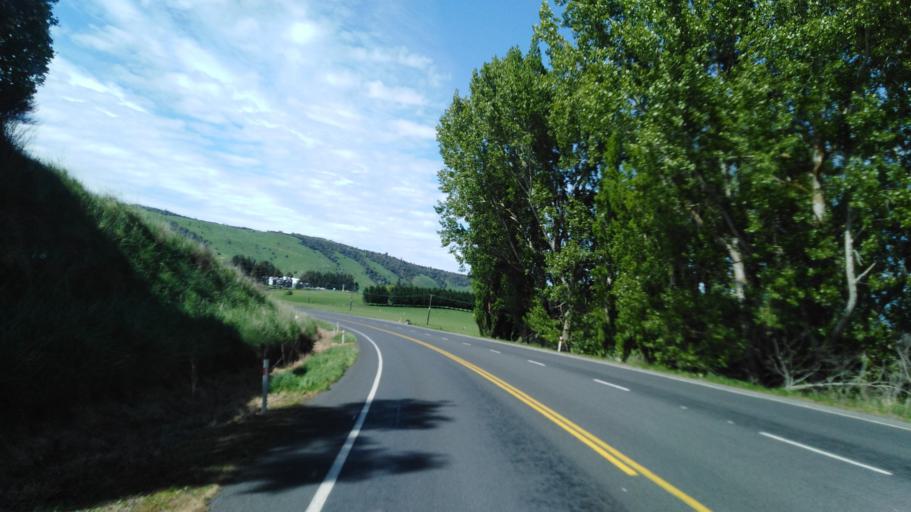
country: NZ
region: Manawatu-Wanganui
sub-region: Ruapehu District
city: Waiouru
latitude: -39.5352
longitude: 175.6801
